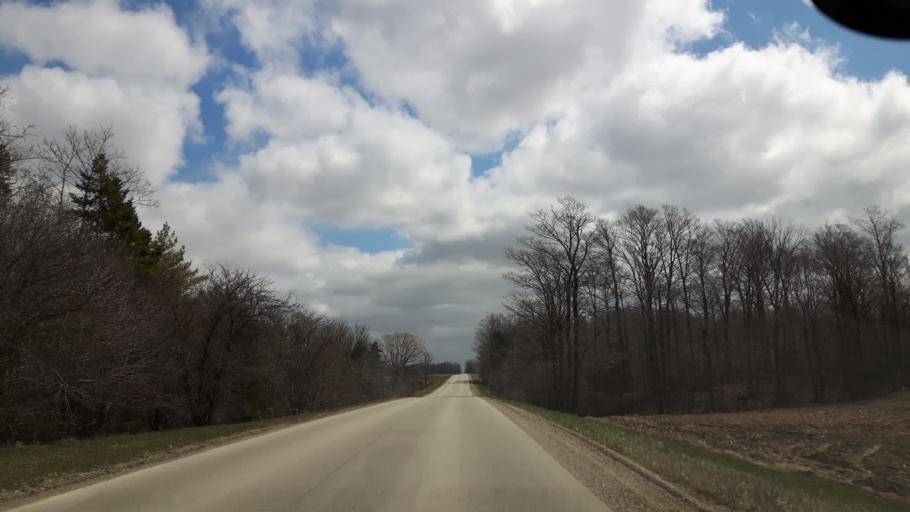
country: CA
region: Ontario
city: Goderich
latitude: 43.6985
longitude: -81.6787
